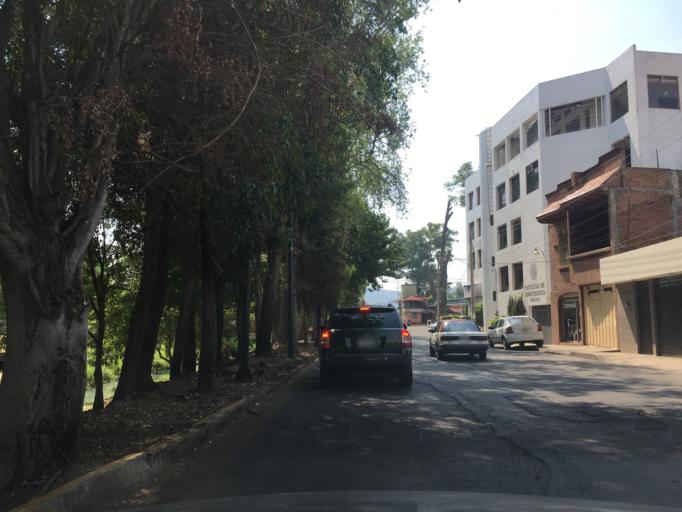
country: MX
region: Michoacan
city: Morelia
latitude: 19.6884
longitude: -101.1816
